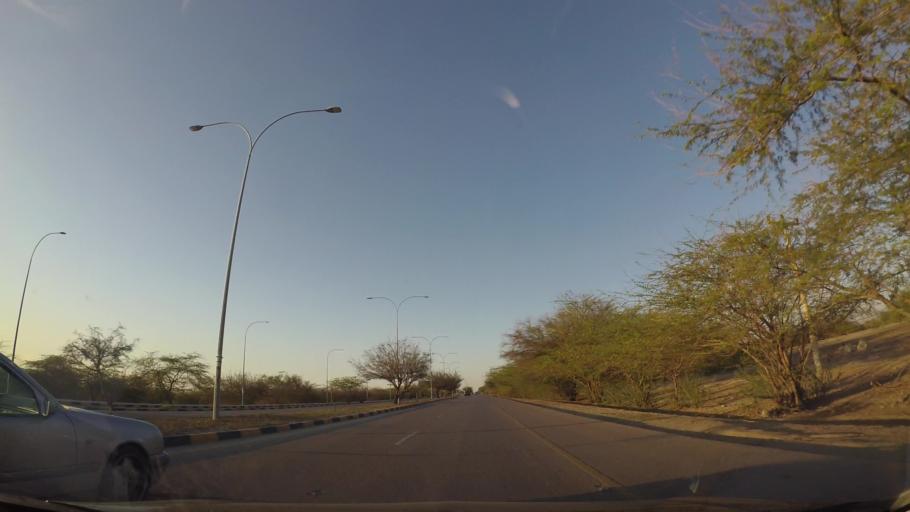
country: PS
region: West Bank
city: Jericho
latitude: 31.7668
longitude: 35.5927
